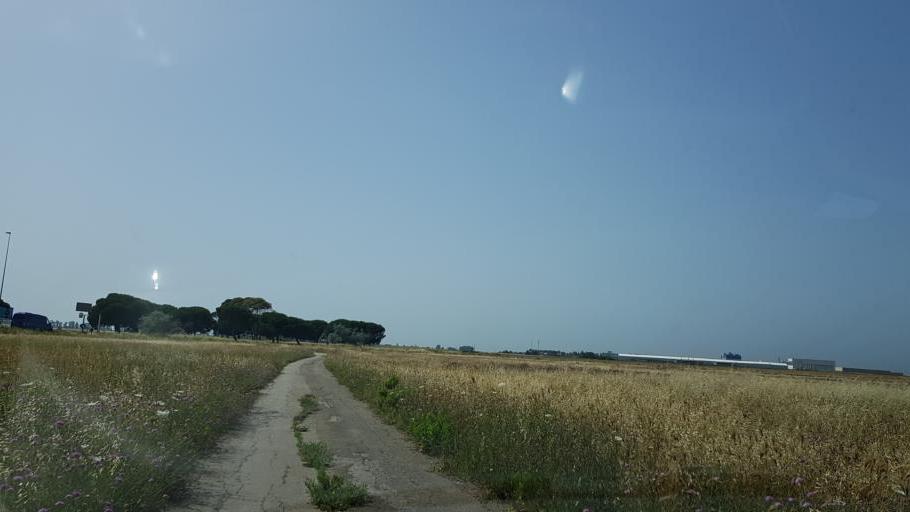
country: IT
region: Apulia
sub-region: Provincia di Brindisi
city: Brindisi
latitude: 40.6639
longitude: 17.9230
